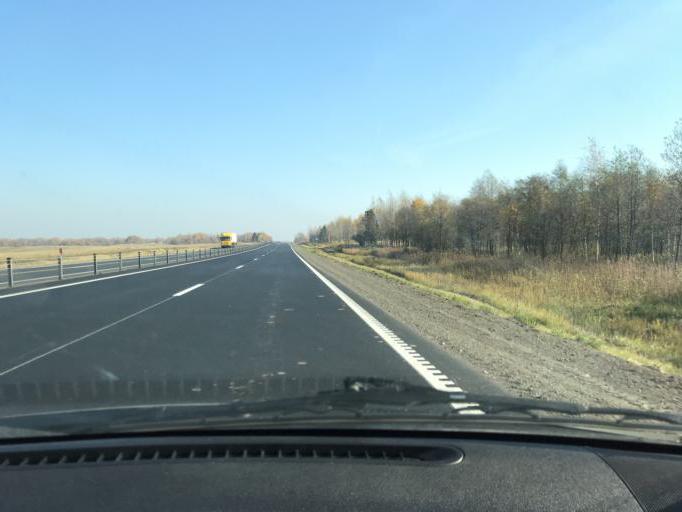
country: BY
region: Vitebsk
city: Dubrowna
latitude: 54.6628
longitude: 30.6784
